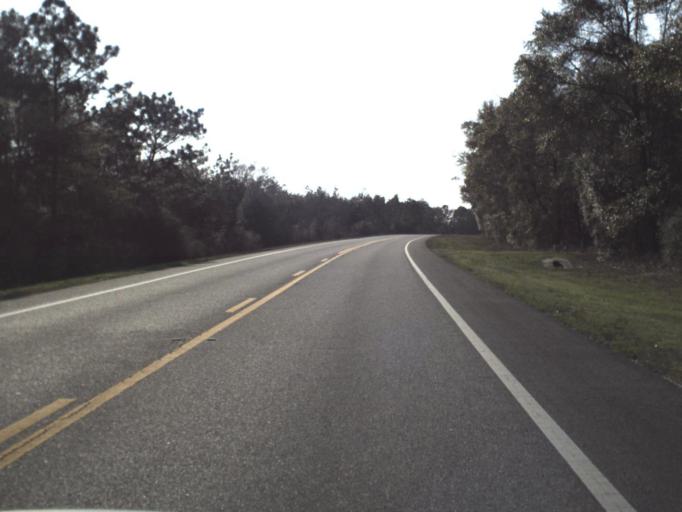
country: US
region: Florida
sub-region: Bay County
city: Youngstown
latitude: 30.4277
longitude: -85.5632
